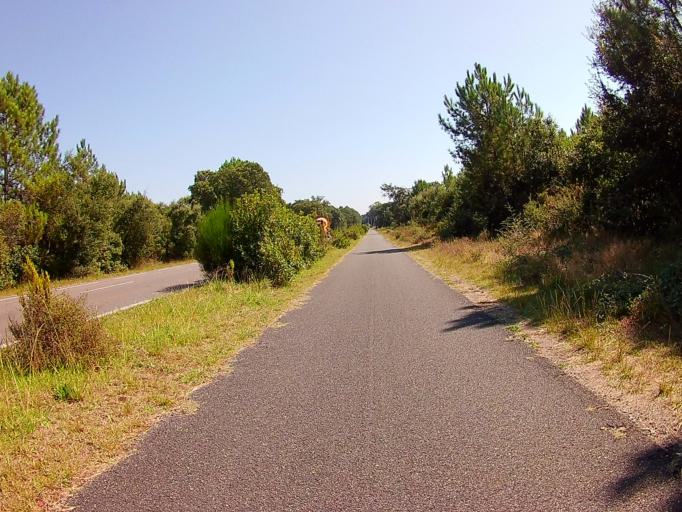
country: FR
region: Aquitaine
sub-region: Departement des Landes
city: Labenne
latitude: 43.5933
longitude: -1.4518
